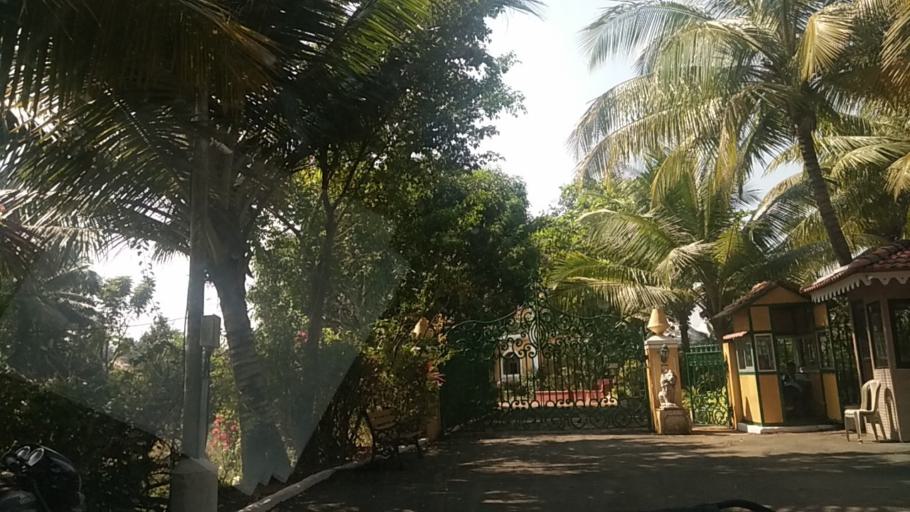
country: IN
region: Goa
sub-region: South Goa
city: Raia
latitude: 15.2974
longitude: 73.9514
